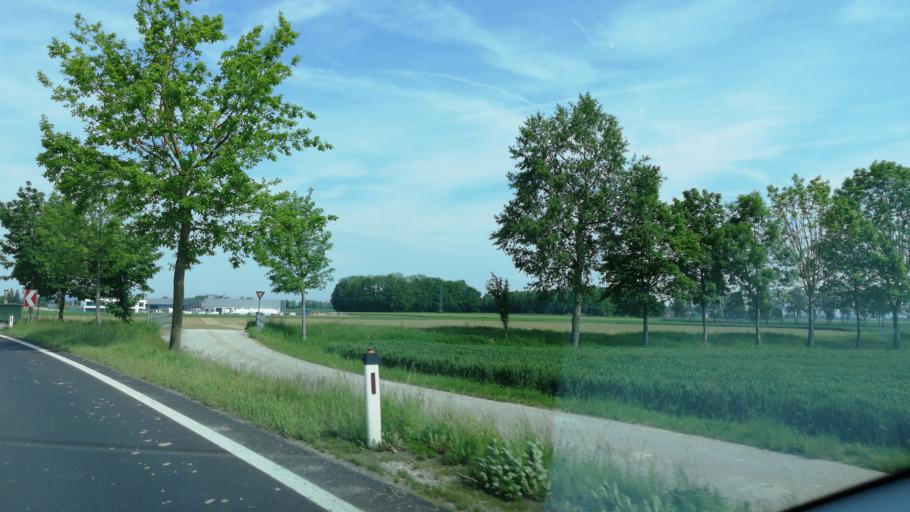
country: DE
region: Bavaria
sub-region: Lower Bavaria
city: Bad Fussing
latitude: 48.3299
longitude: 13.3732
